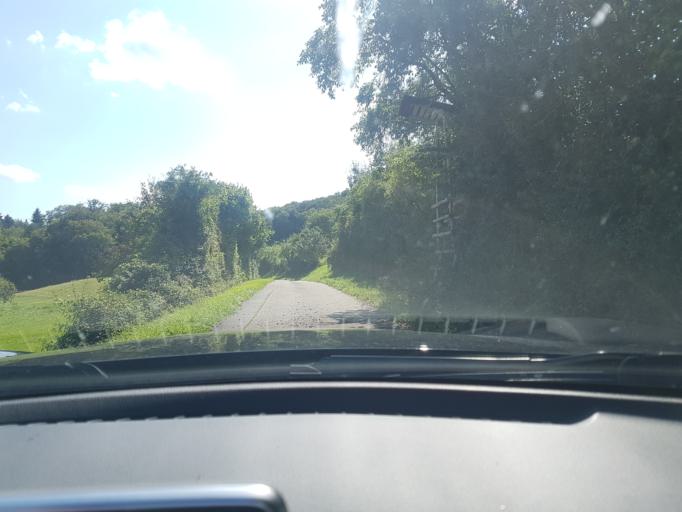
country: DE
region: Baden-Wuerttemberg
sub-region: Regierungsbezirk Stuttgart
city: Widdern
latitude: 49.3487
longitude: 9.4225
